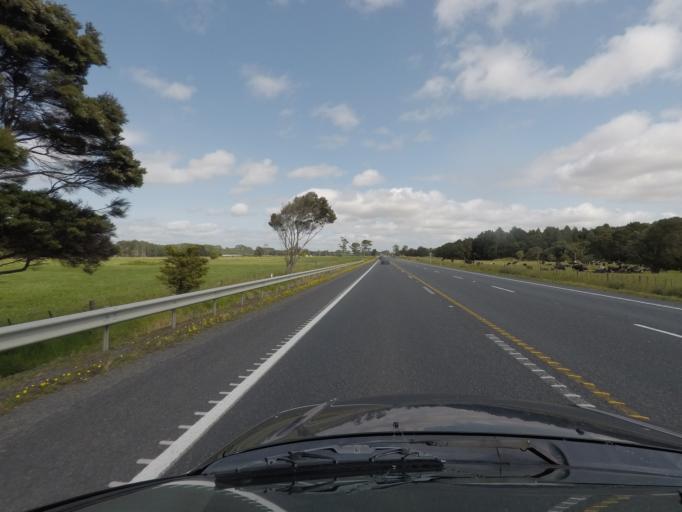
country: NZ
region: Northland
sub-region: Whangarei
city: Ruakaka
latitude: -35.8730
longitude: 174.4060
